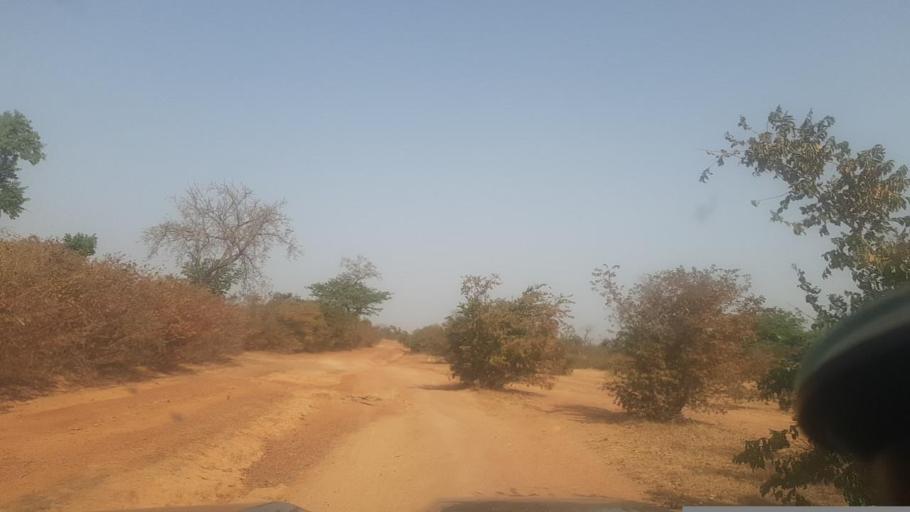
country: ML
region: Segou
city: Bla
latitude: 12.8562
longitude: -5.9740
